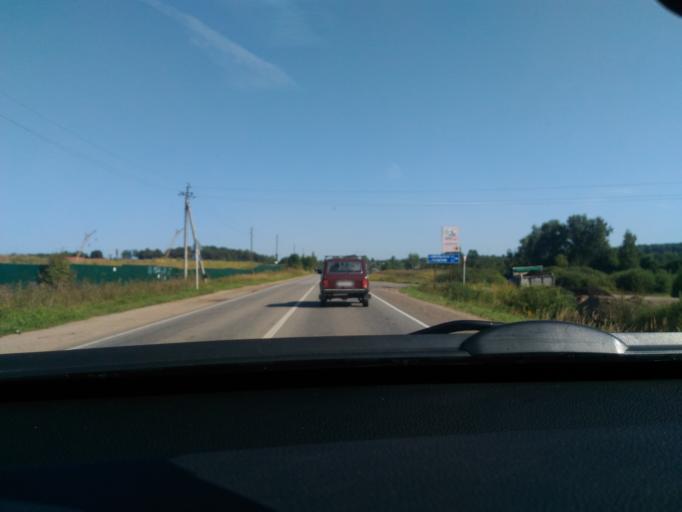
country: RU
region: Moskovskaya
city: Podosinki
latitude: 56.2231
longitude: 37.5485
